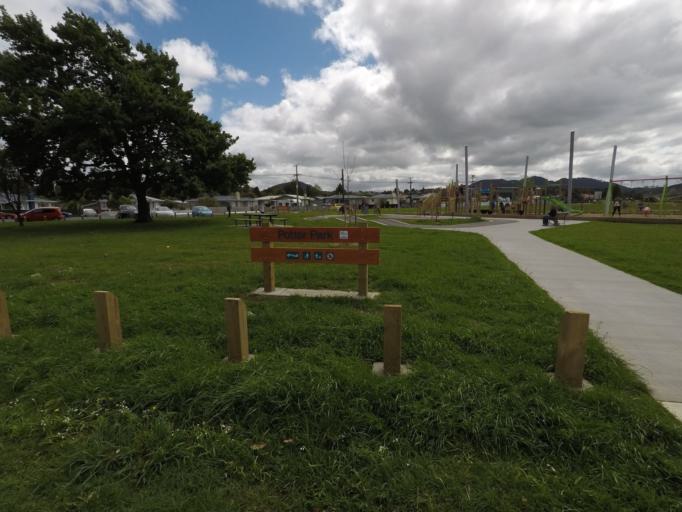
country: NZ
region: Northland
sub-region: Whangarei
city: Whangarei
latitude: -35.6805
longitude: 174.3253
